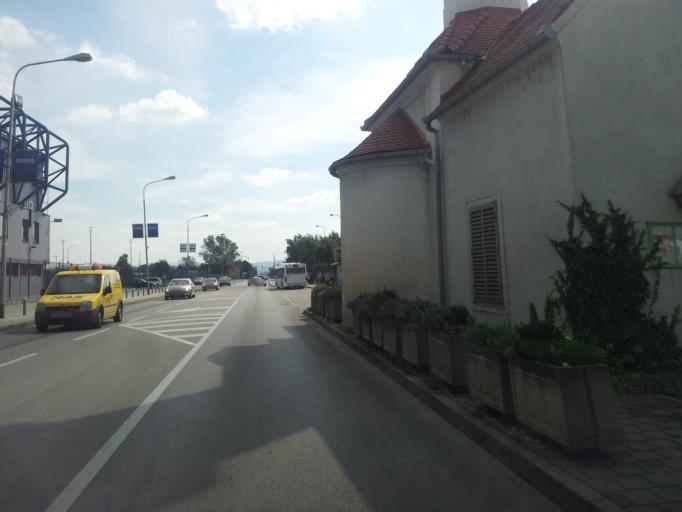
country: HR
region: Varazdinska
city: Varazdin
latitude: 46.2933
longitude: 16.3435
